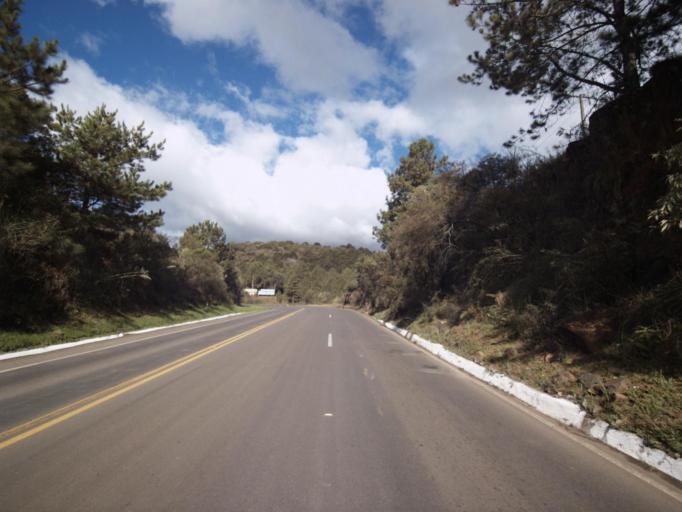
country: BR
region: Santa Catarina
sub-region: Joacaba
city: Joacaba
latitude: -27.0593
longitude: -51.6801
